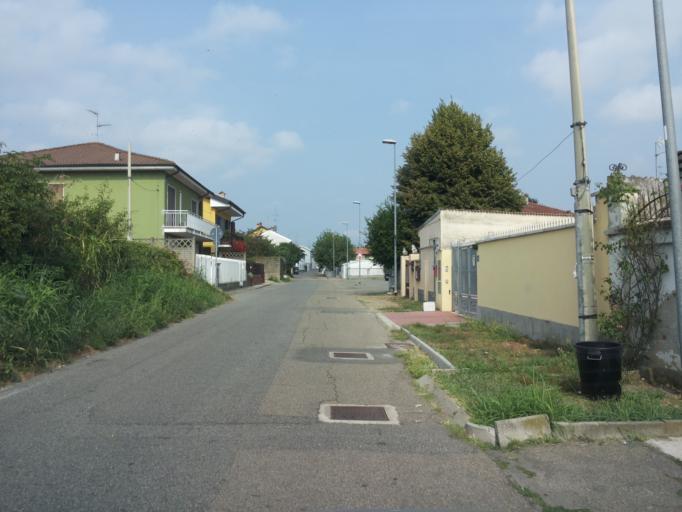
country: IT
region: Piedmont
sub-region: Provincia di Vercelli
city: Prarolo
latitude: 45.3043
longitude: 8.4523
